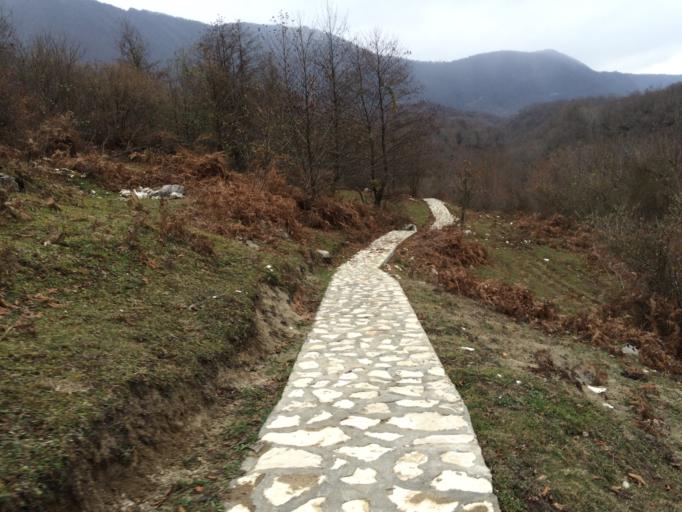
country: GE
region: Imereti
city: Tsqaltubo
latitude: 42.4563
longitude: 42.5465
